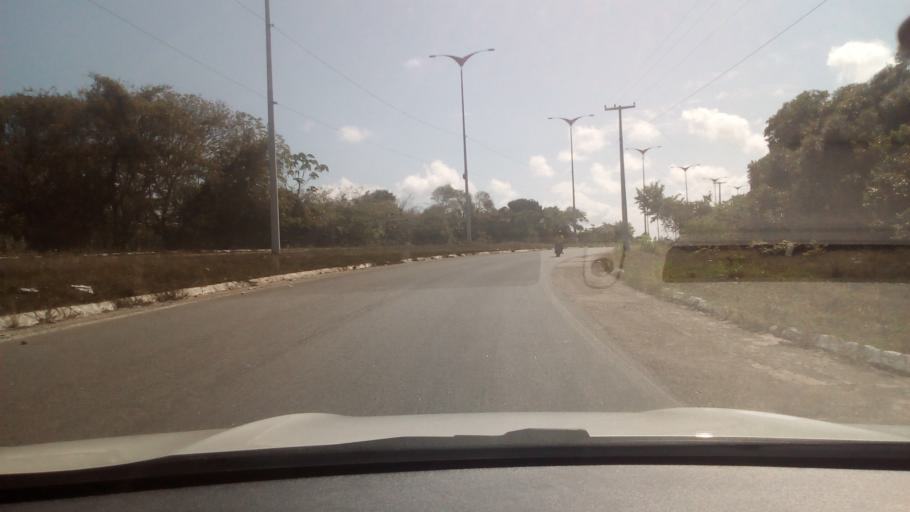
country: BR
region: Paraiba
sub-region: Joao Pessoa
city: Joao Pessoa
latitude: -7.1763
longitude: -34.8015
